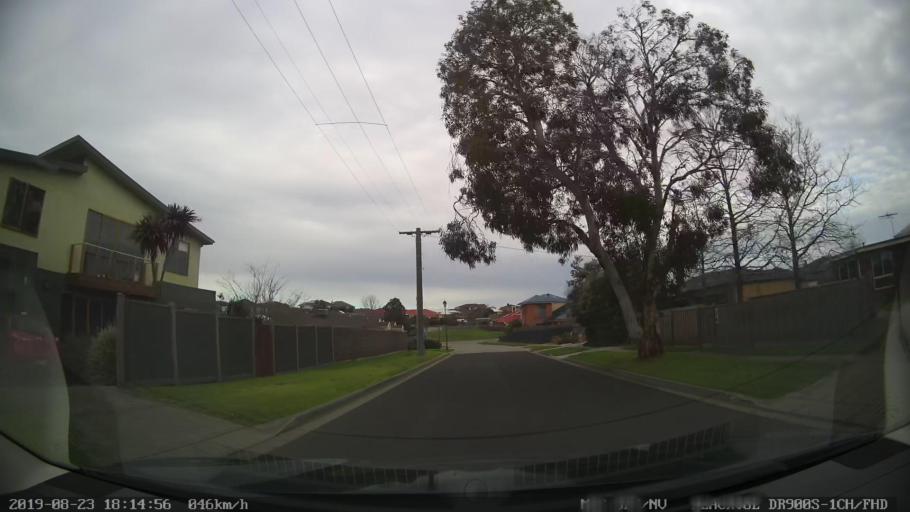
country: AU
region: Victoria
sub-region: Mornington Peninsula
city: Mornington
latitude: -38.2360
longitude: 145.0438
